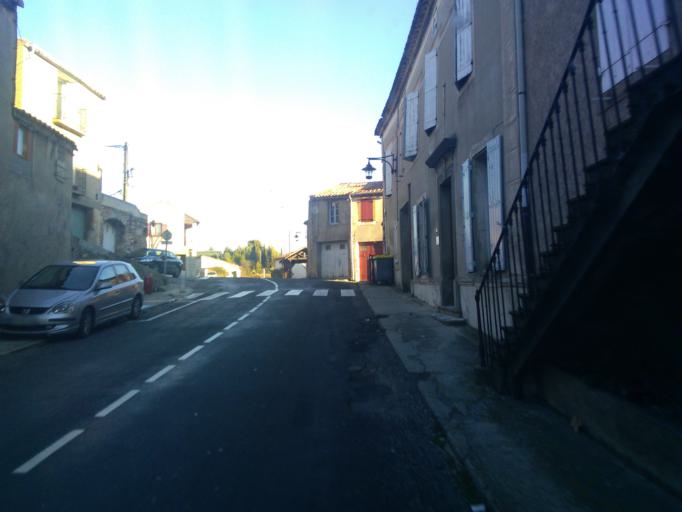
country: FR
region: Languedoc-Roussillon
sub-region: Departement de l'Aude
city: Caunes-Minervois
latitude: 43.3279
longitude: 2.5298
